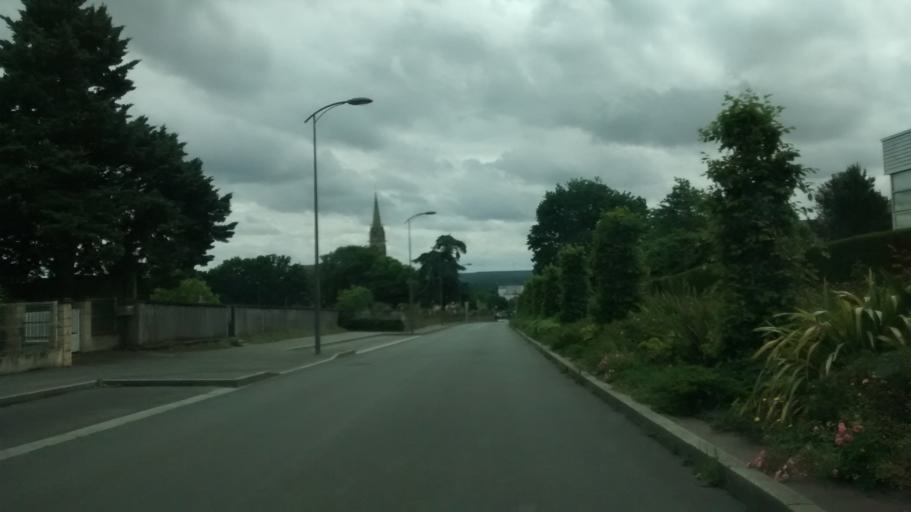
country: FR
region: Brittany
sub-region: Departement du Morbihan
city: Carentoir
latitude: 47.8193
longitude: -2.1310
